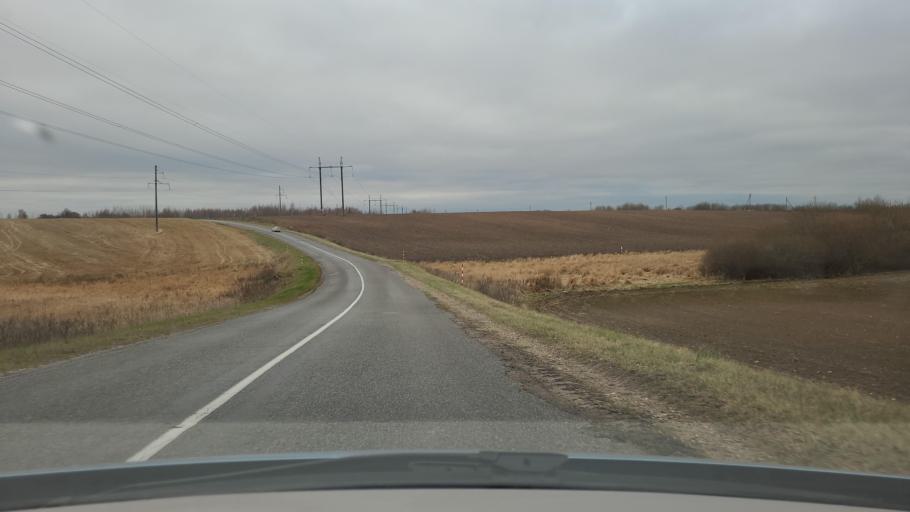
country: BY
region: Minsk
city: Khalopyenichy
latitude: 54.5525
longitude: 28.9843
